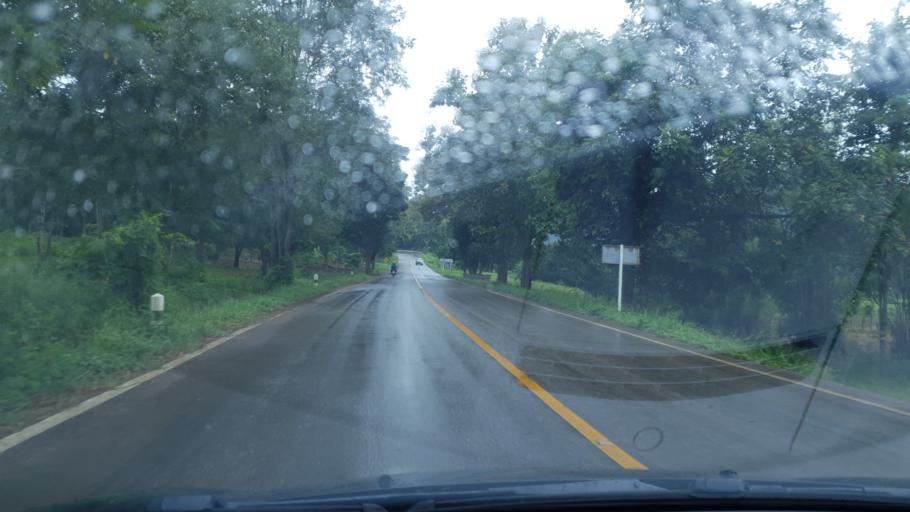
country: TH
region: Mae Hong Son
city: Mae La Noi
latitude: 18.5194
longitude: 97.9299
